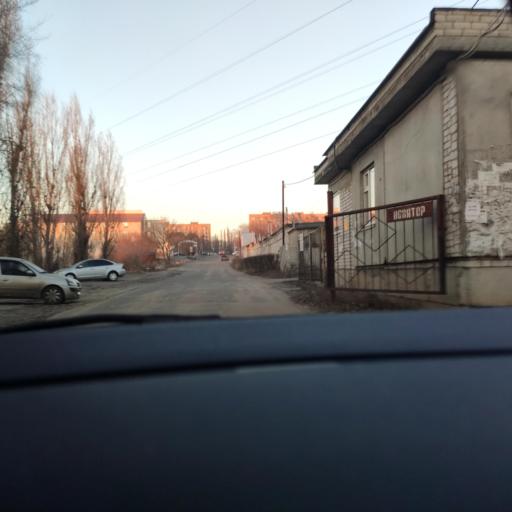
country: RU
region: Voronezj
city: Pridonskoy
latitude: 51.6444
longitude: 39.1224
